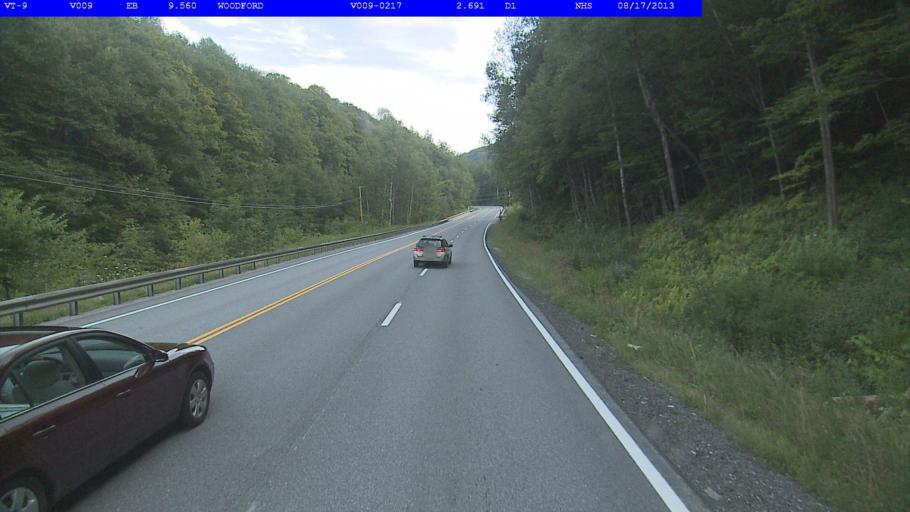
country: US
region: Vermont
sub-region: Bennington County
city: Bennington
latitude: 42.8824
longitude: -73.1162
